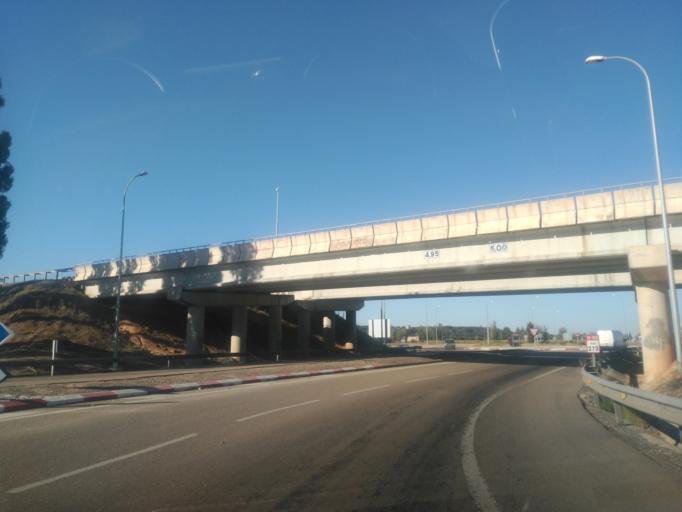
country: ES
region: Castille and Leon
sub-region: Provincia de Burgos
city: Villalba de Duero
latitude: 41.6647
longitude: -3.7281
